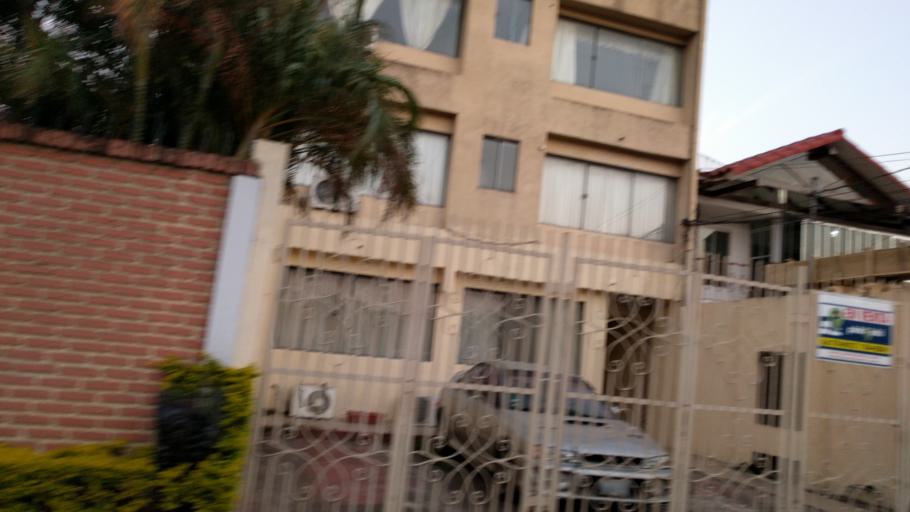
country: BO
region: Santa Cruz
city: Santa Cruz de la Sierra
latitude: -17.7692
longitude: -63.1583
